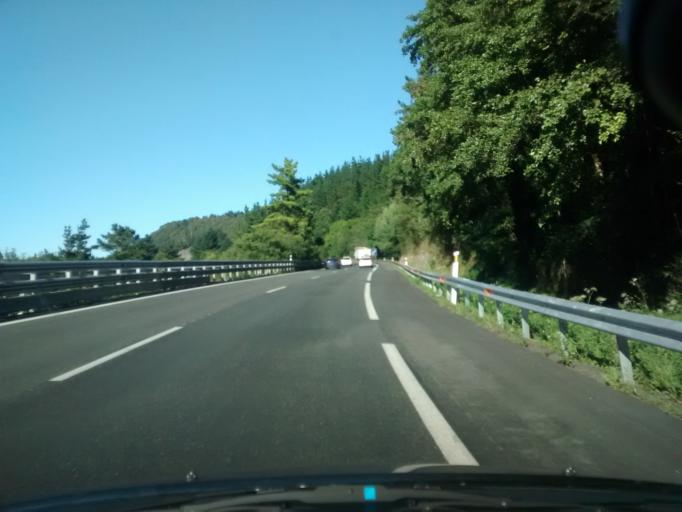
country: ES
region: Basque Country
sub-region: Provincia de Guipuzcoa
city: Mendaro
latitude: 43.2700
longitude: -2.3704
